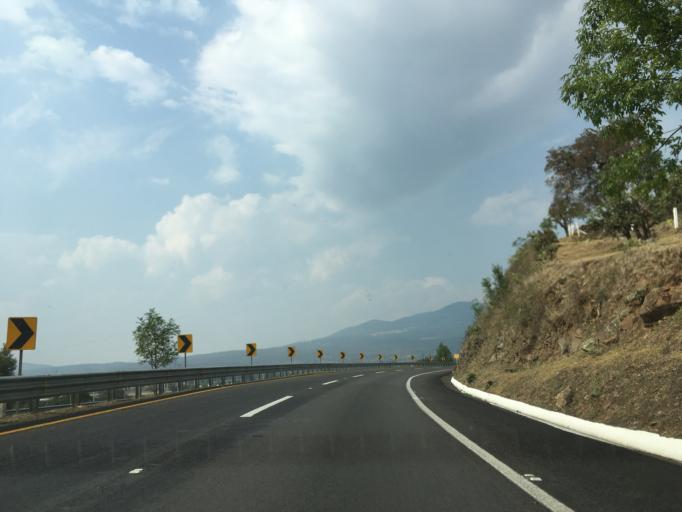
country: MX
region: Michoacan
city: Huiramba
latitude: 19.5520
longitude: -101.4306
